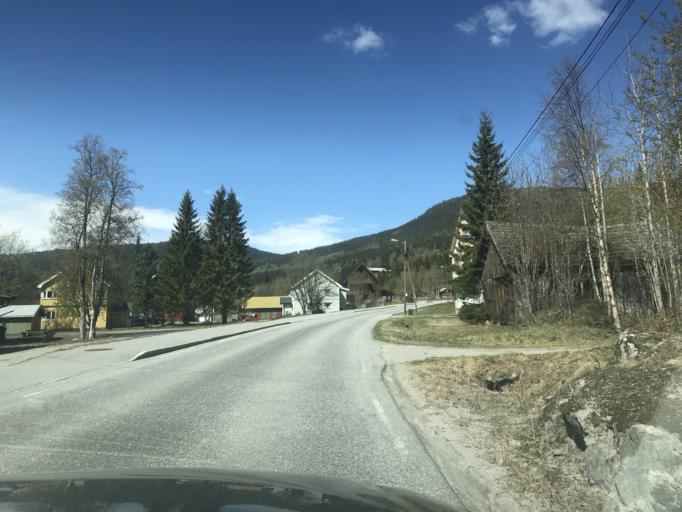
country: NO
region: Telemark
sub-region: Hjartdal
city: Sauland
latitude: 59.7520
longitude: 8.7973
